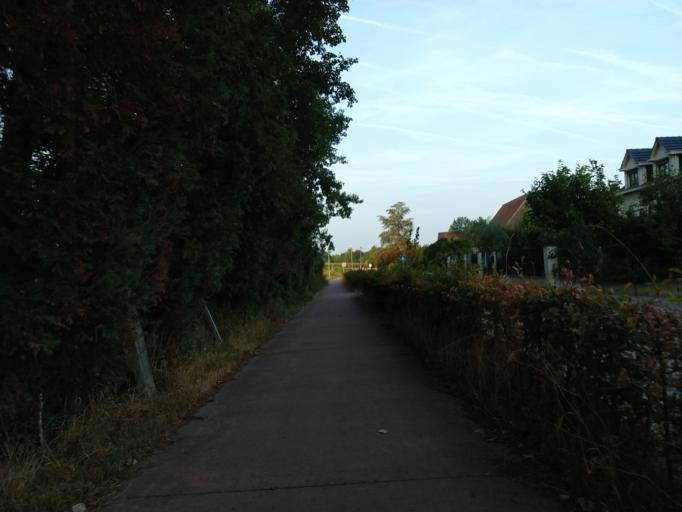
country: BE
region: Flanders
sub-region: Provincie Vlaams-Brabant
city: Tienen
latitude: 50.7863
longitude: 4.9272
